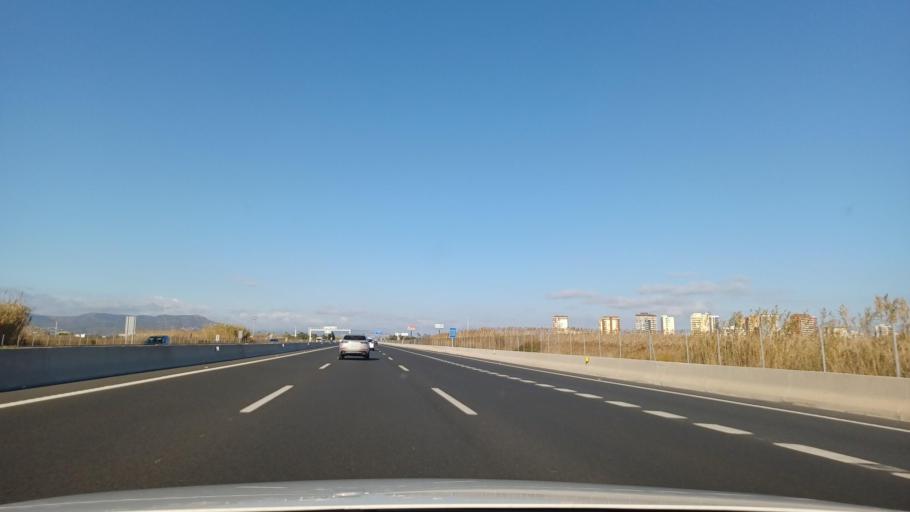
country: ES
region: Valencia
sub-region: Provincia de Valencia
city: Albuixech
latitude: 39.5540
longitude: -0.2979
